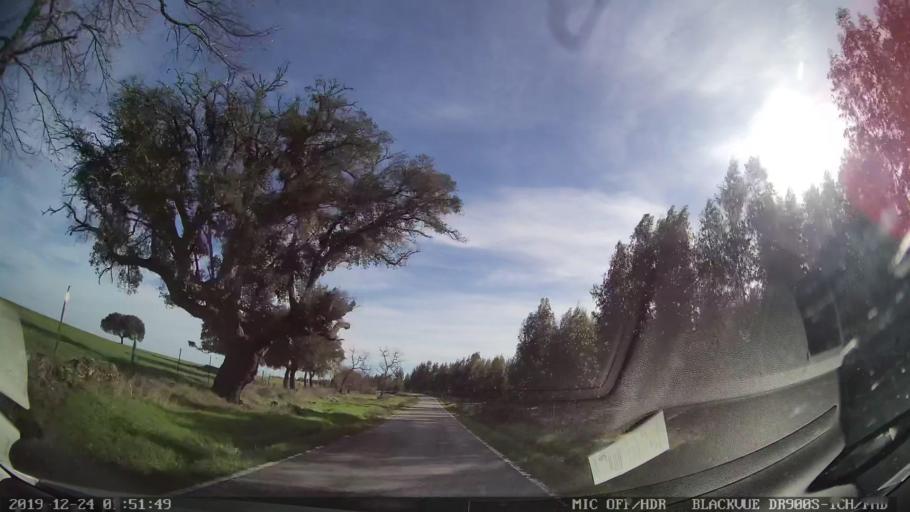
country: PT
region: Portalegre
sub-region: Nisa
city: Nisa
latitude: 39.4947
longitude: -7.7534
